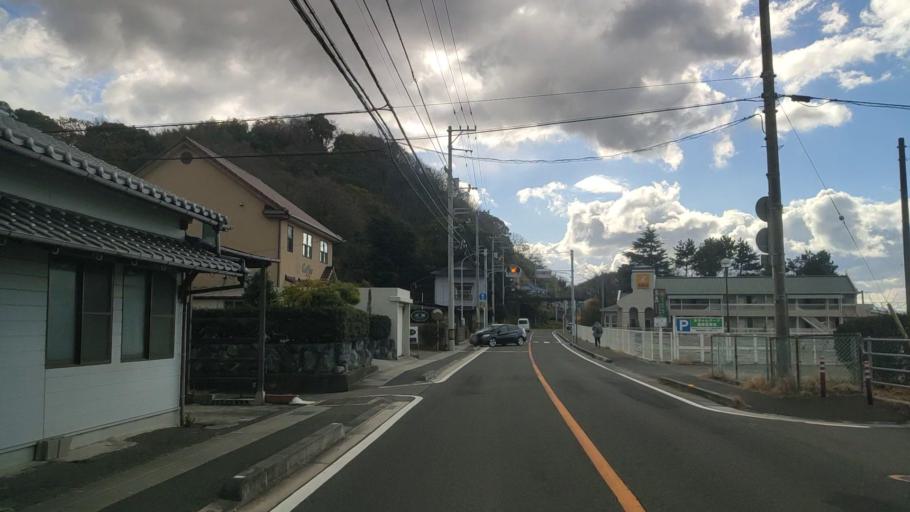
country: JP
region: Ehime
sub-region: Shikoku-chuo Shi
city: Matsuyama
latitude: 33.8746
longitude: 132.7084
